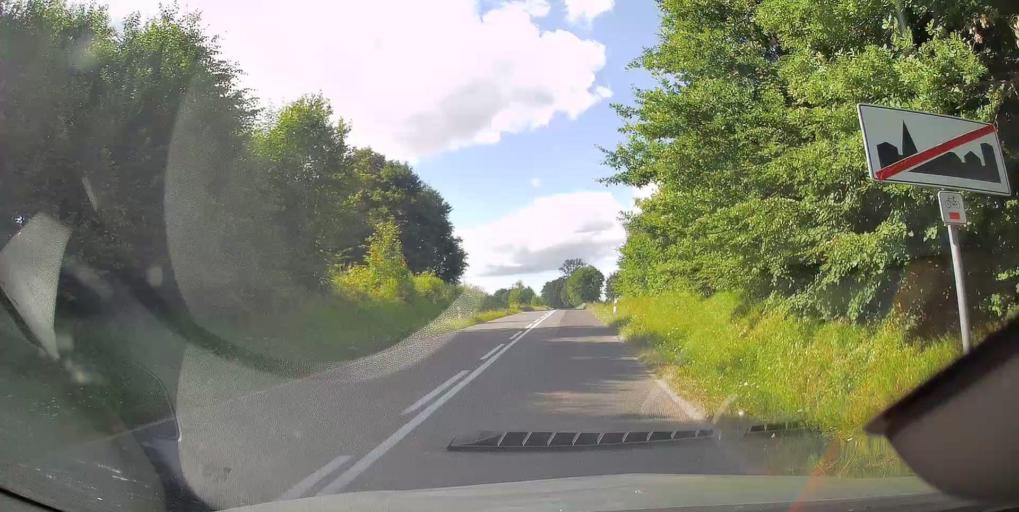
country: PL
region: Swietokrzyskie
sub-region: Powiat kielecki
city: Nowa Slupia
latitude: 50.8853
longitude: 21.0463
